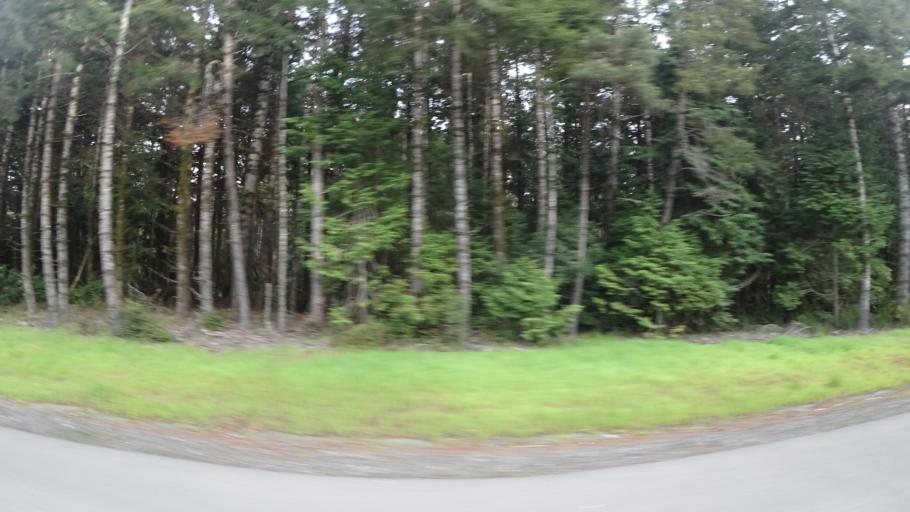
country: US
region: Oregon
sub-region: Coos County
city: Bandon
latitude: 43.1709
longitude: -124.3759
